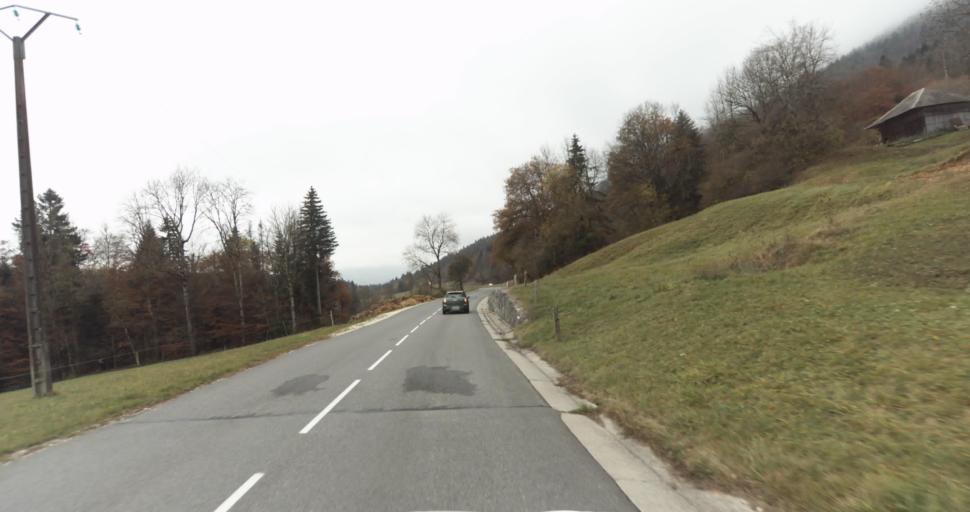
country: FR
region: Rhone-Alpes
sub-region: Departement de la Haute-Savoie
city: Gruffy
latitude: 45.7611
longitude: 6.1205
